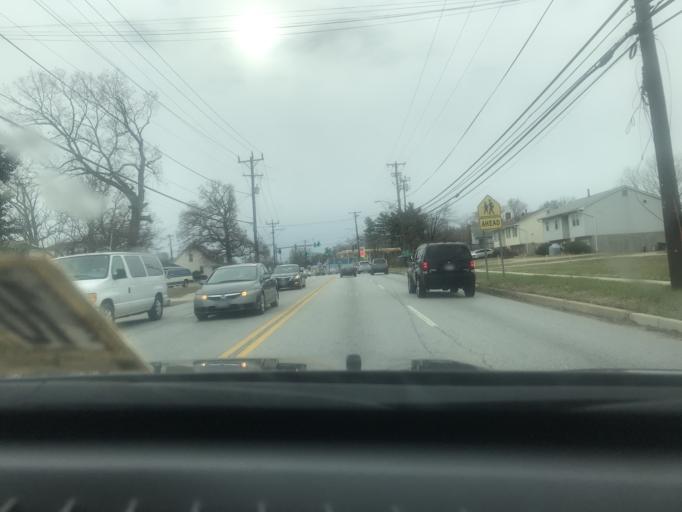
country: US
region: Maryland
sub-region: Prince George's County
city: Temple Hills
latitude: 38.7887
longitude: -76.9376
